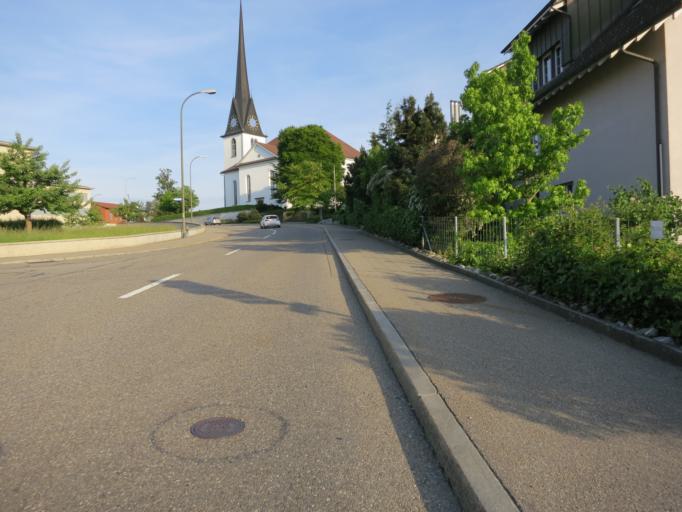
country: CH
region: Zurich
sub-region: Bezirk Hinwil
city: Gossau
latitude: 47.3018
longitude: 8.7614
